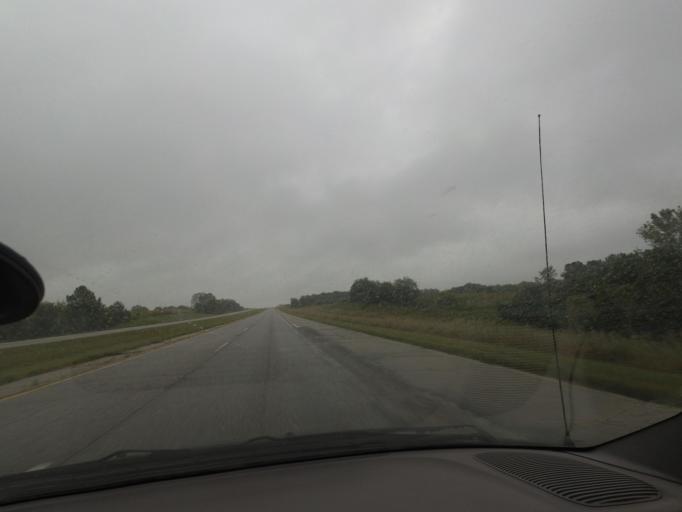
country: US
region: Illinois
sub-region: Pike County
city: Barry
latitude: 39.6924
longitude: -90.9840
